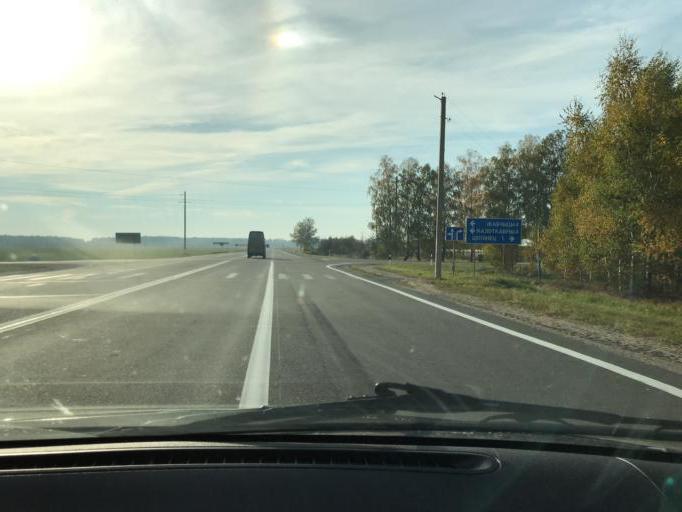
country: BY
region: Brest
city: Horad Pinsk
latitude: 52.1516
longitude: 25.9245
